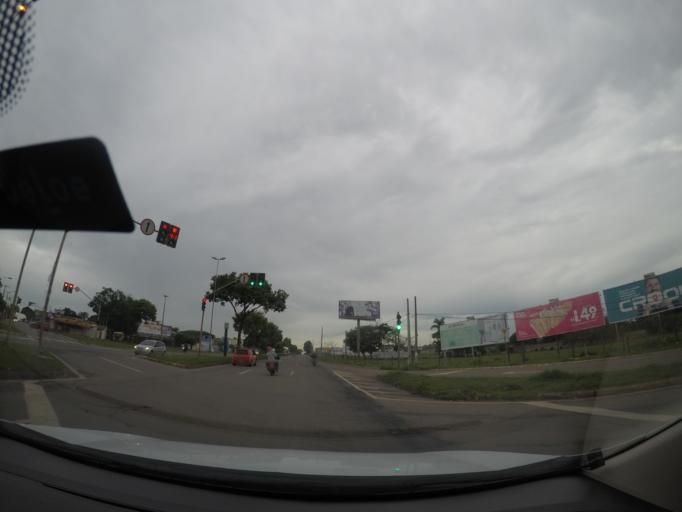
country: BR
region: Goias
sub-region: Goiania
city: Goiania
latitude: -16.6349
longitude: -49.2829
